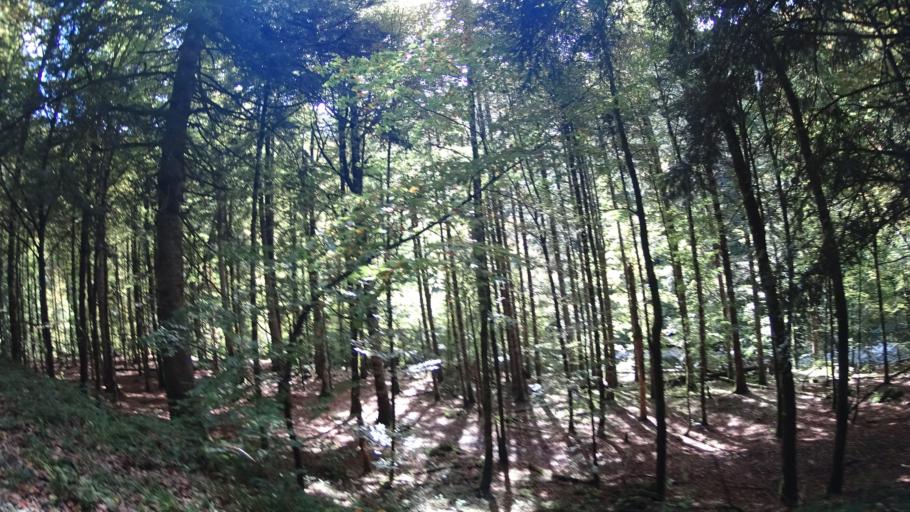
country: ES
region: Navarre
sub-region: Provincia de Navarra
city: Orbara
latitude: 42.9829
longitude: -1.1262
